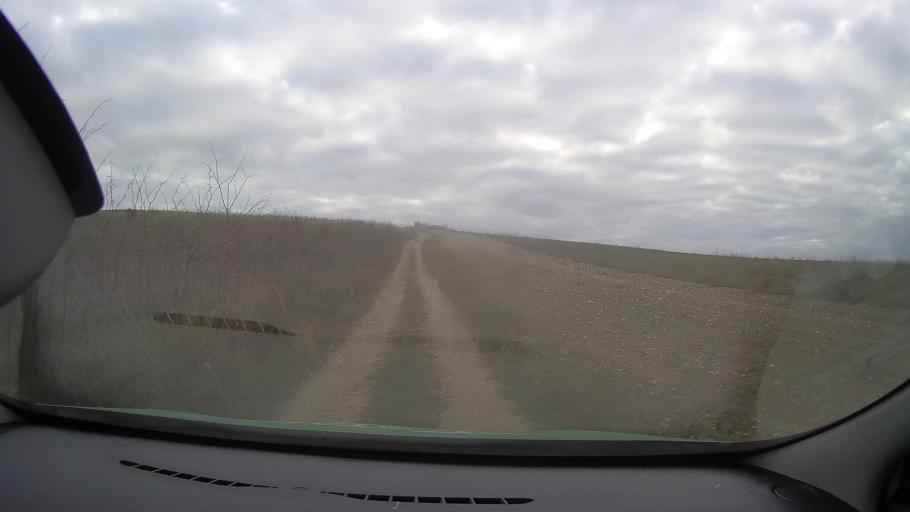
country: RO
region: Tulcea
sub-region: Comuna Jurilovca
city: Jurilovca
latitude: 44.7686
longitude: 28.9147
